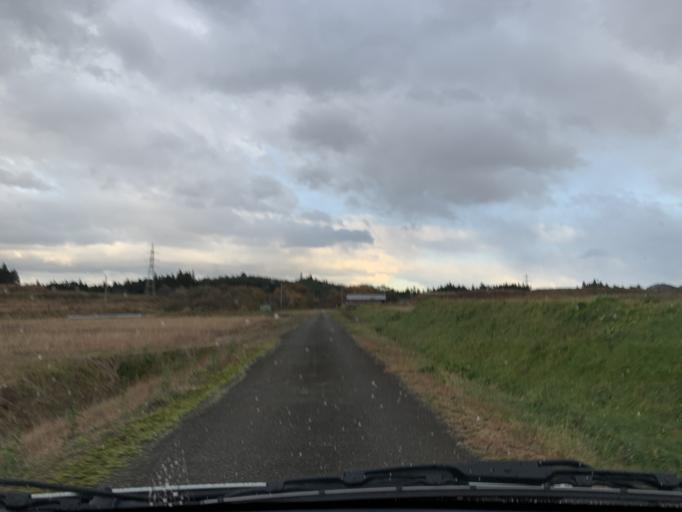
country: JP
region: Iwate
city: Mizusawa
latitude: 39.0858
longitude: 141.0035
